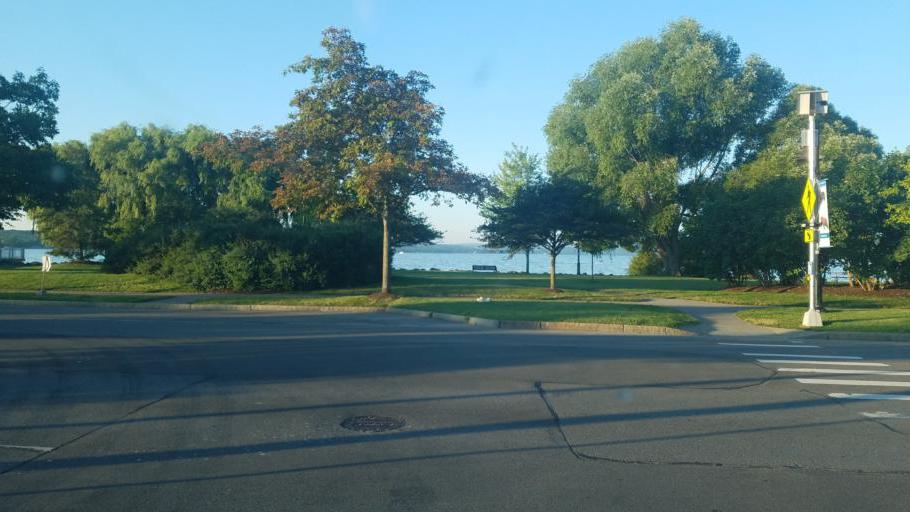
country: US
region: New York
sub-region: Ontario County
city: Canandaigua
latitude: 42.8757
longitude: -77.2688
